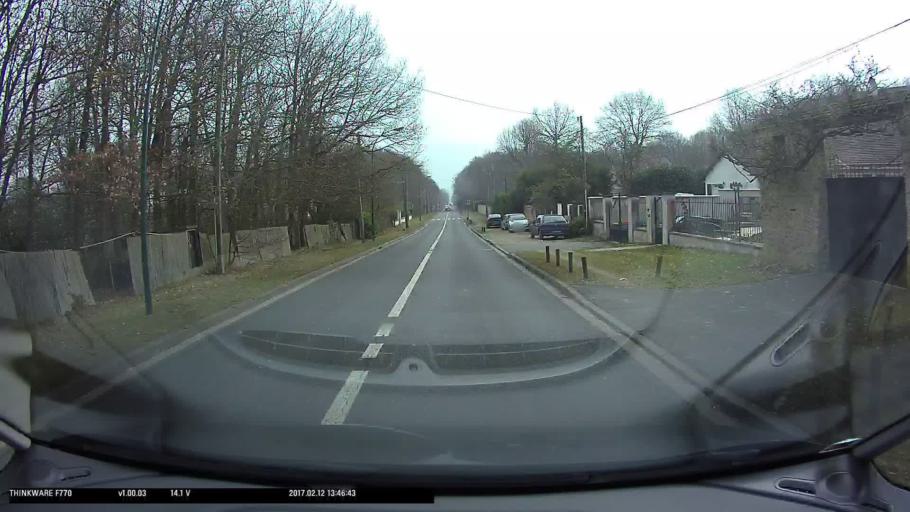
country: FR
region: Ile-de-France
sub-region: Departement du Val-d'Oise
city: Courdimanche
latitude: 49.0155
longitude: 1.9993
